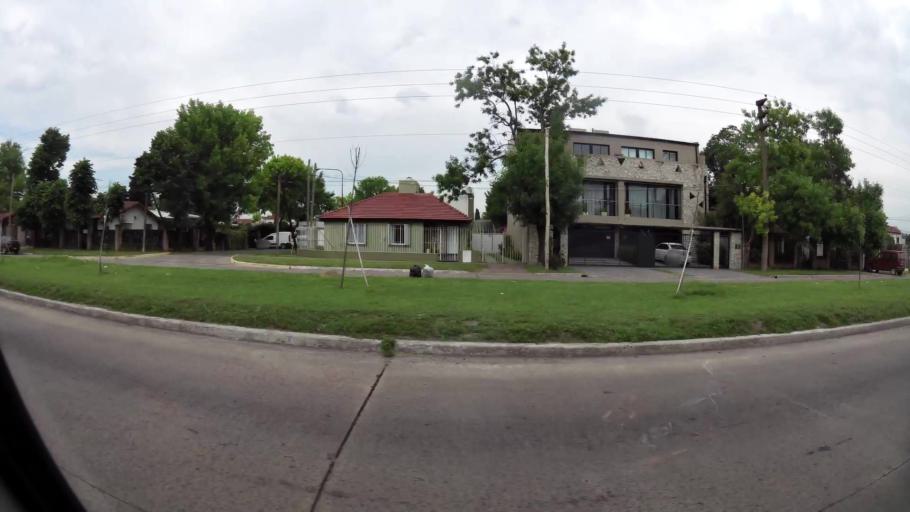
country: AR
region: Buenos Aires
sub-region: Partido de La Plata
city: La Plata
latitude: -34.8999
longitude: -57.9839
